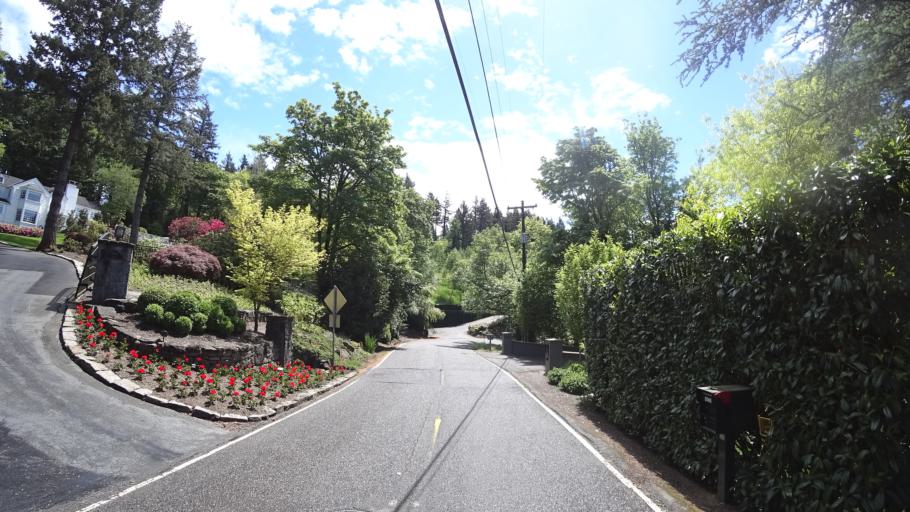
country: US
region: Oregon
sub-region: Washington County
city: West Slope
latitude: 45.5067
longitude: -122.7348
